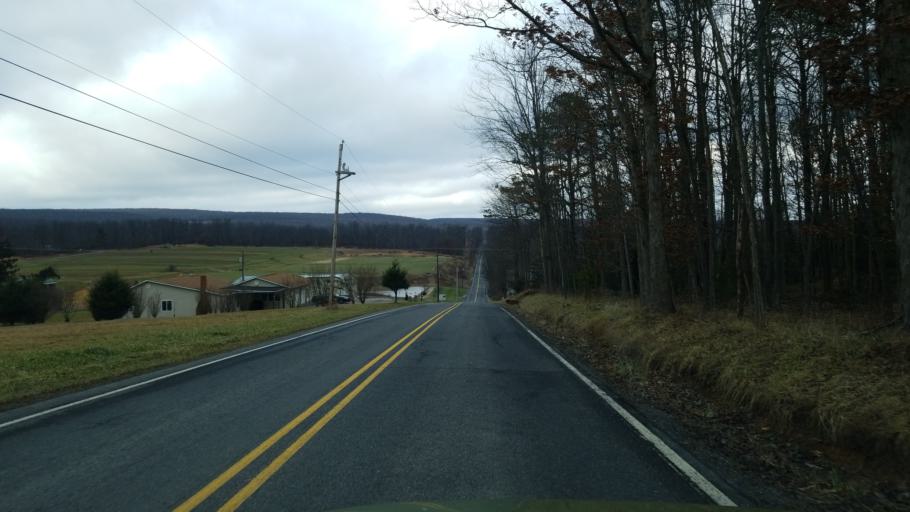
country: US
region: Pennsylvania
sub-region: Clearfield County
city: Hyde
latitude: 41.0414
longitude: -78.4892
